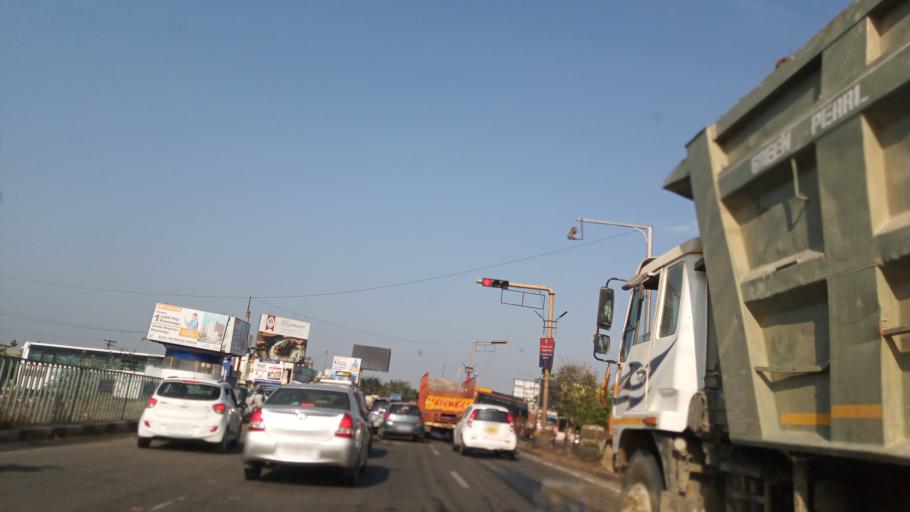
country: IN
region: Tamil Nadu
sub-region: Kancheepuram
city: Poonamalle
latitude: 13.0454
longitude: 80.0696
